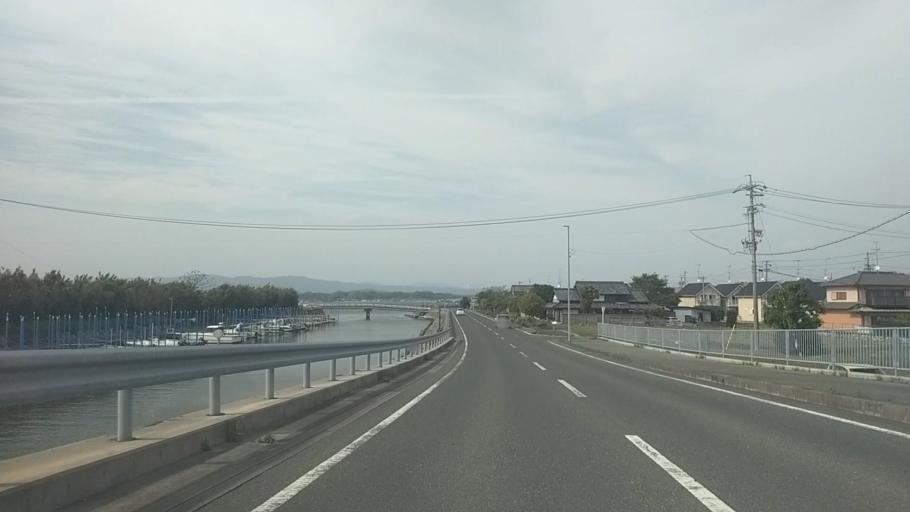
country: JP
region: Shizuoka
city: Kosai-shi
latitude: 34.7109
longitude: 137.6191
